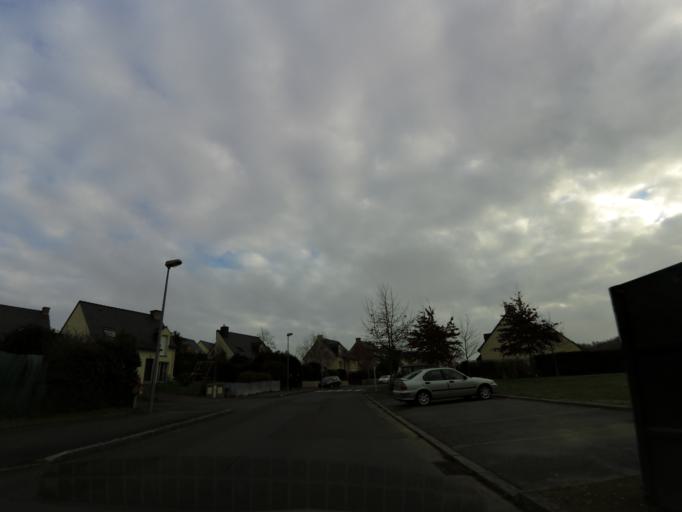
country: FR
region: Brittany
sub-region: Departement d'Ille-et-Vilaine
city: Orgeres
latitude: 47.9922
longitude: -1.6678
